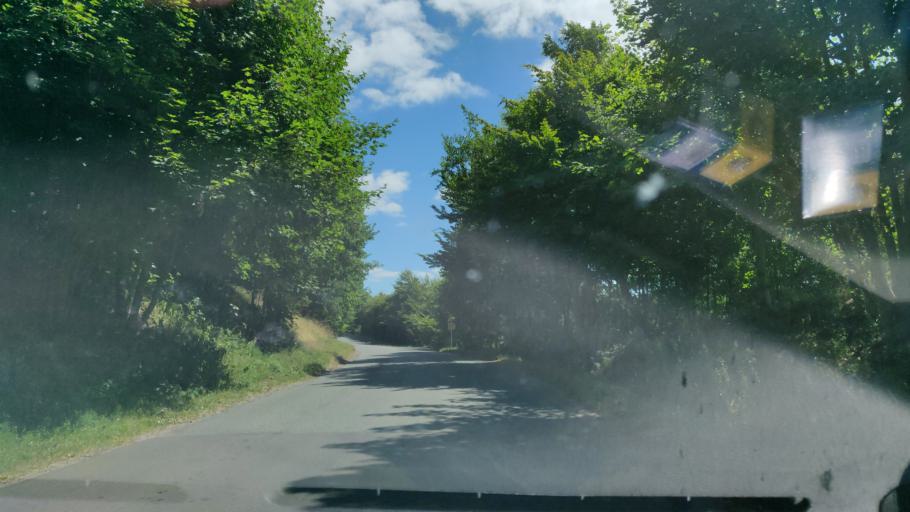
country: DK
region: South Denmark
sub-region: Kolding Kommune
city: Kolding
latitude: 55.5412
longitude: 9.5167
